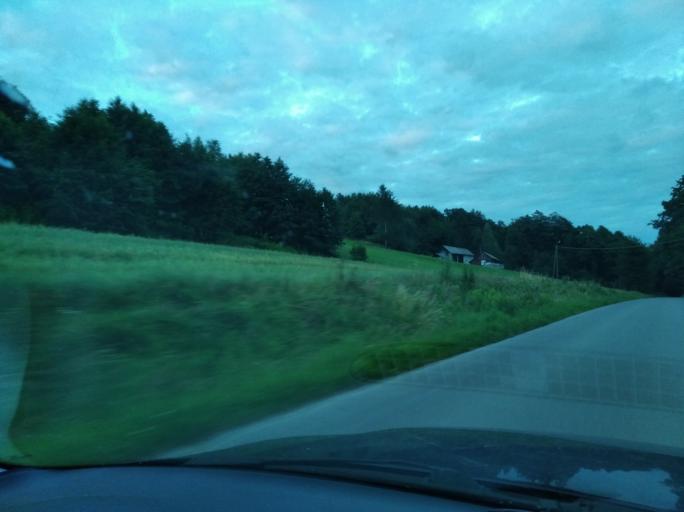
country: PL
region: Subcarpathian Voivodeship
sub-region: Powiat ropczycko-sedziszowski
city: Zagorzyce
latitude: 49.9924
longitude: 21.7180
